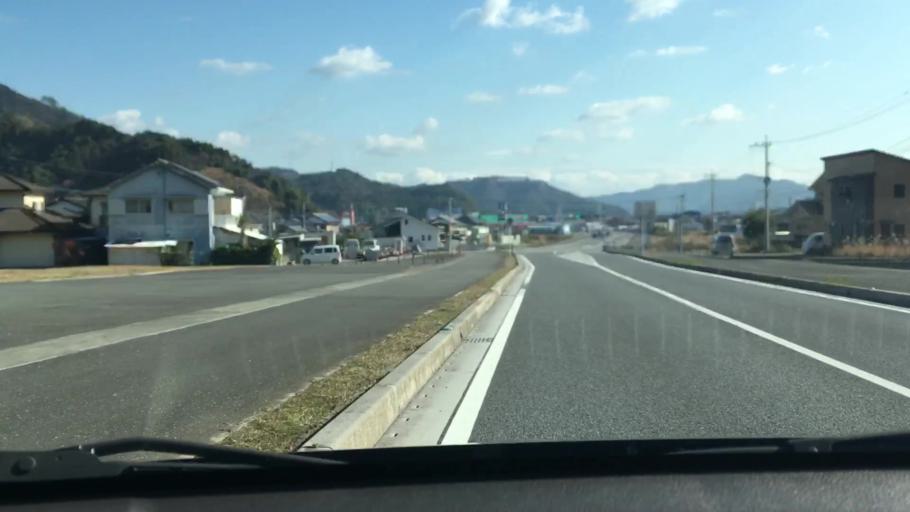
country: JP
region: Oita
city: Saiki
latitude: 32.9616
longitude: 131.8572
